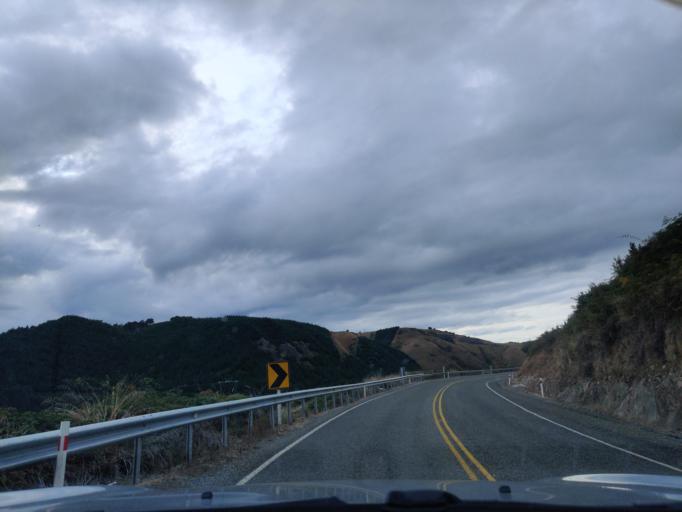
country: NZ
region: Tasman
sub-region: Tasman District
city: Wakefield
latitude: -41.7032
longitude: 172.6668
